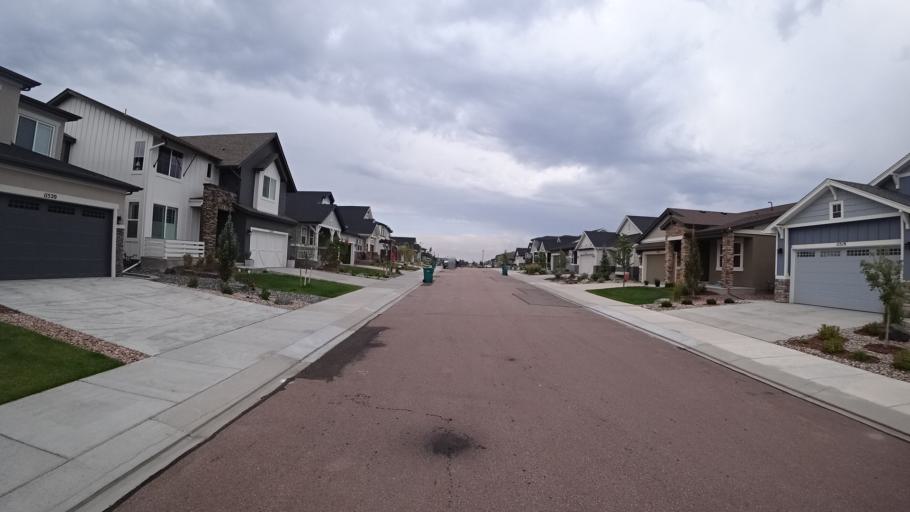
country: US
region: Colorado
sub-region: El Paso County
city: Gleneagle
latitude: 39.0034
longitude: -104.8033
